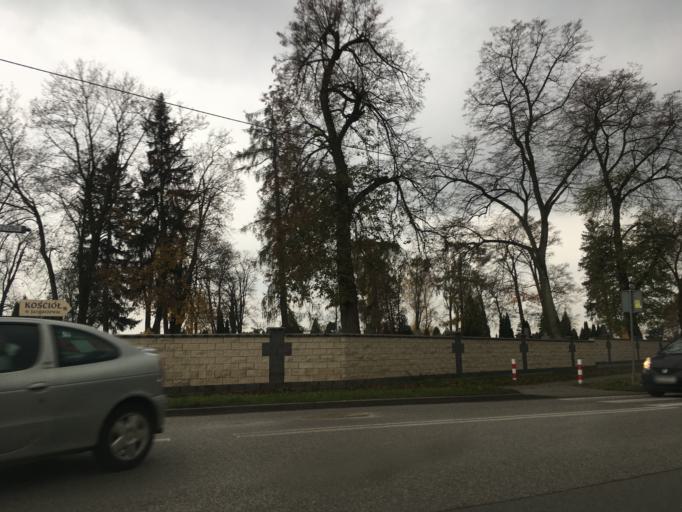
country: PL
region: Masovian Voivodeship
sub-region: Powiat piaseczynski
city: Zalesie Gorne
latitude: 52.0410
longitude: 21.0022
